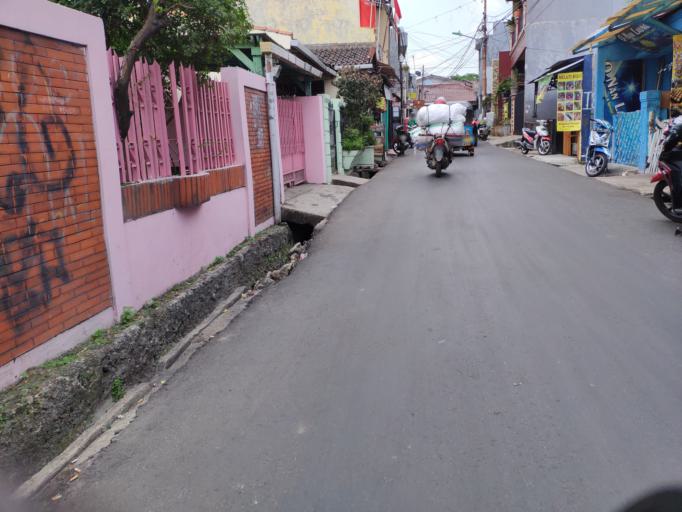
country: ID
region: Jakarta Raya
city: Jakarta
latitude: -6.2114
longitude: 106.8657
